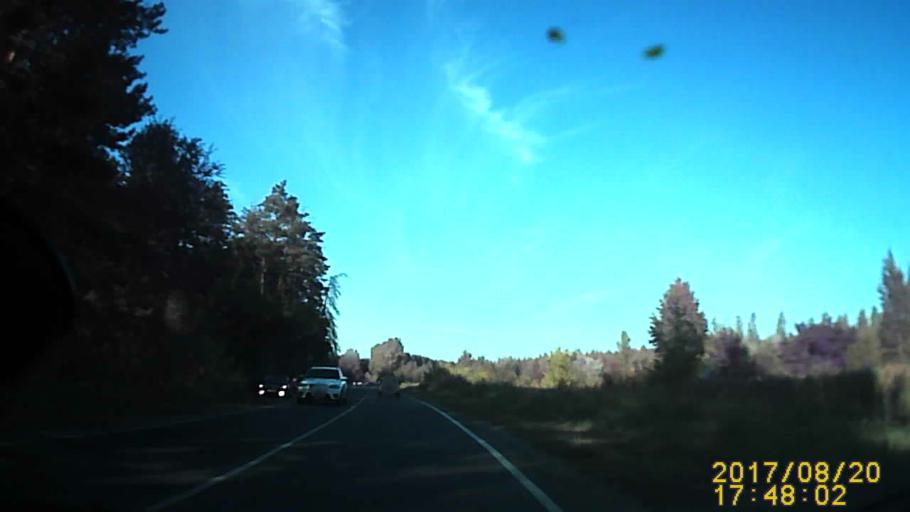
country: RU
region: Ulyanovsk
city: Mirnyy
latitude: 54.4196
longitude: 48.7872
